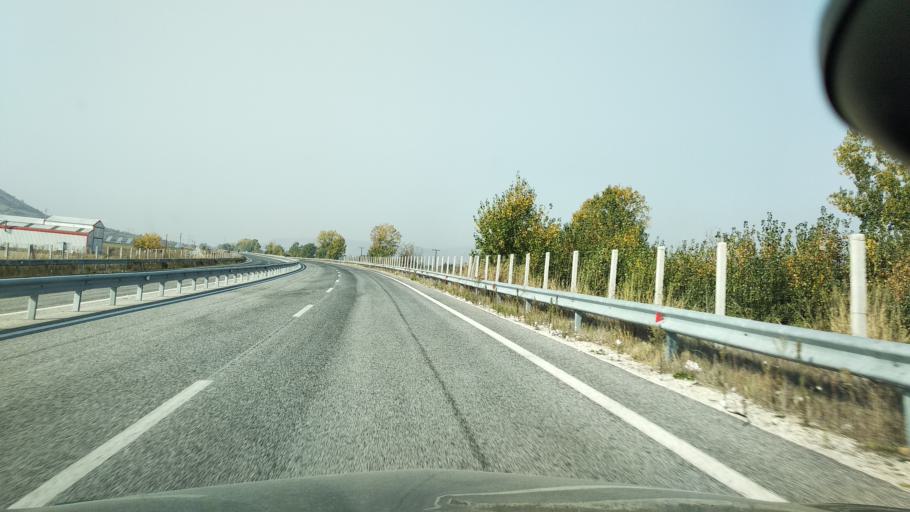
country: GR
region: Thessaly
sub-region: Trikala
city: Farkadona
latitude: 39.5851
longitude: 22.0407
